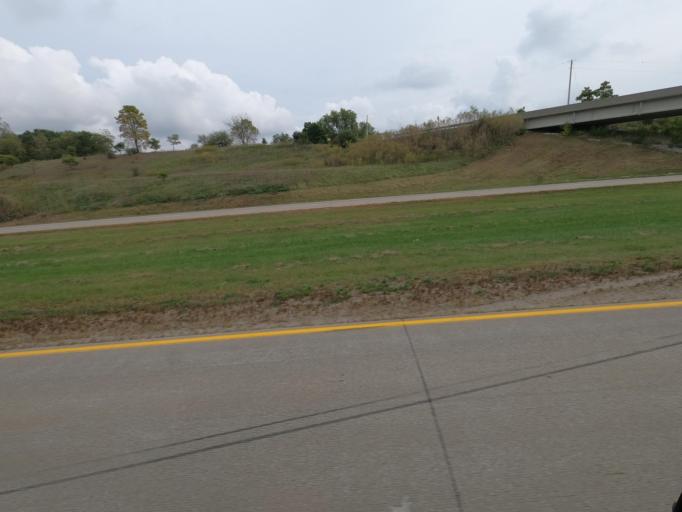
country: US
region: Iowa
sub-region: Wapello County
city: Ottumwa
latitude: 41.0356
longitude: -92.3749
